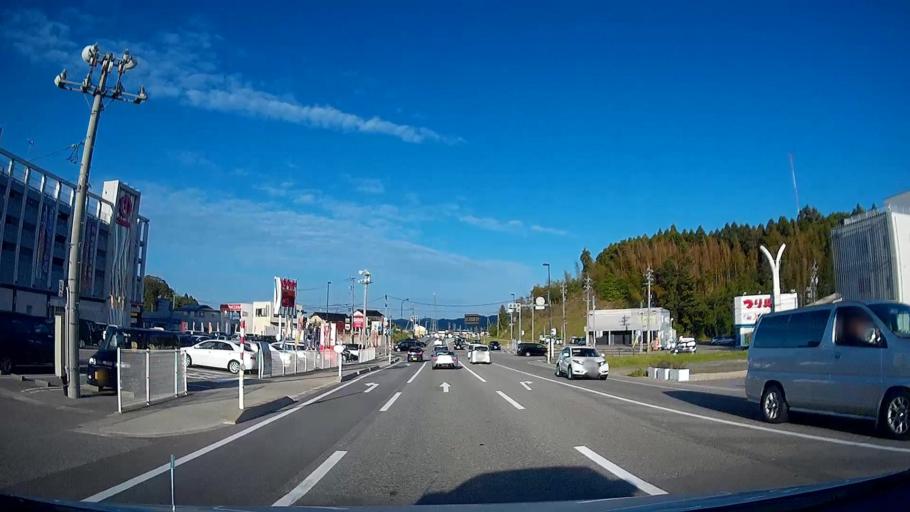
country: JP
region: Ishikawa
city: Nanao
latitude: 37.0343
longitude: 136.9513
